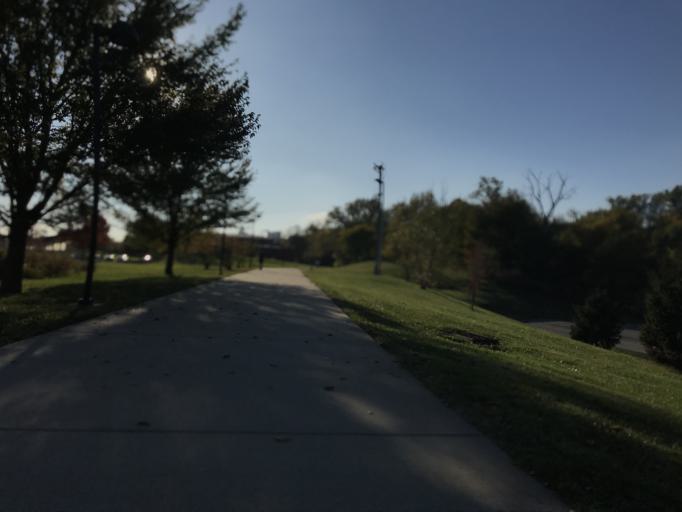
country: US
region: Indiana
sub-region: Clark County
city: Jeffersonville
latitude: 38.2648
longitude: -85.7292
